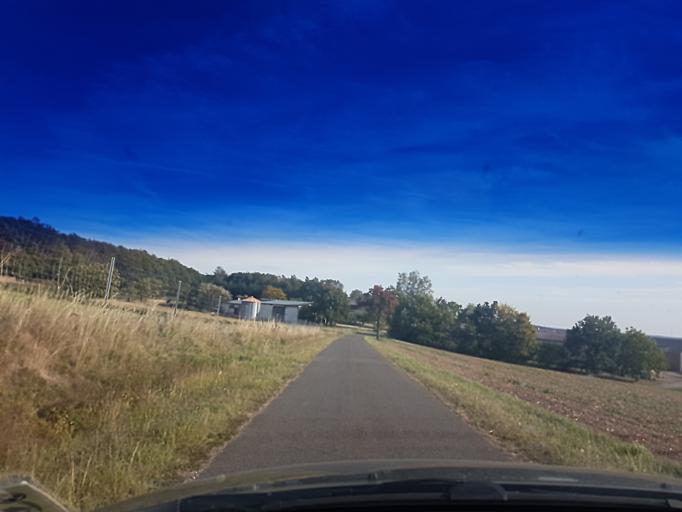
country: DE
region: Bavaria
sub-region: Regierungsbezirk Unterfranken
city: Geiselwind
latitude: 49.7855
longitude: 10.5391
